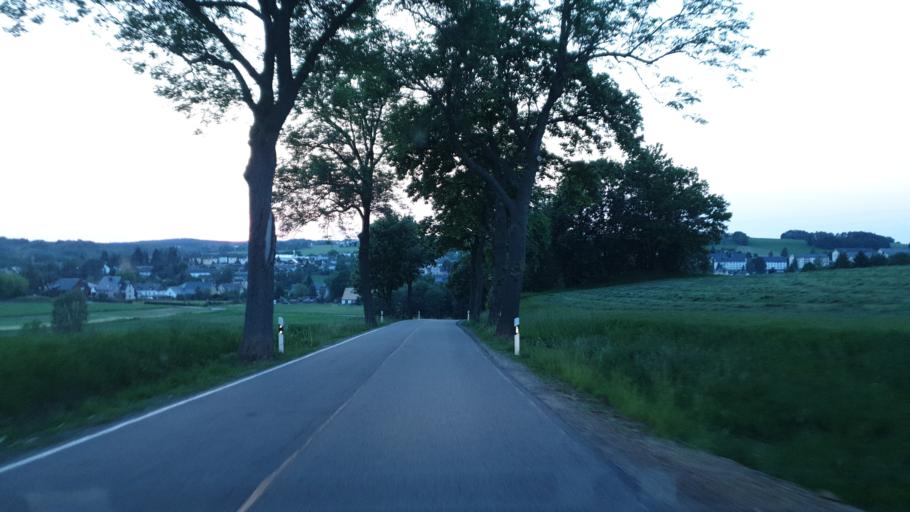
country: DE
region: Saxony
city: Zschorlau
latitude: 50.5584
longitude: 12.6465
